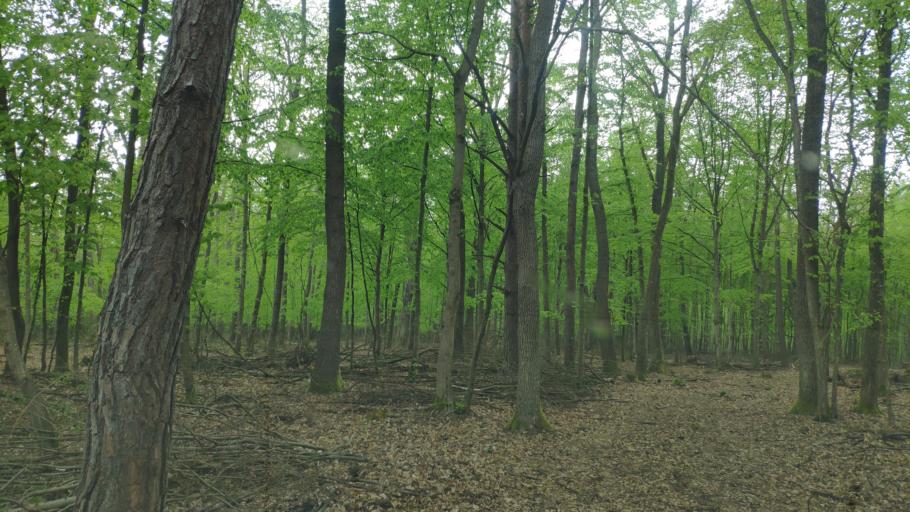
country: SK
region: Kosicky
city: Moldava nad Bodvou
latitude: 48.5485
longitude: 20.9304
